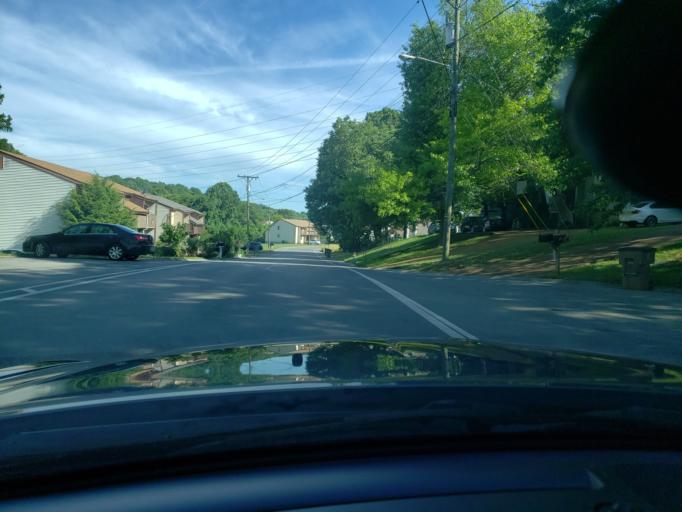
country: US
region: Tennessee
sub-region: Williamson County
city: Nolensville
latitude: 36.0378
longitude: -86.6722
